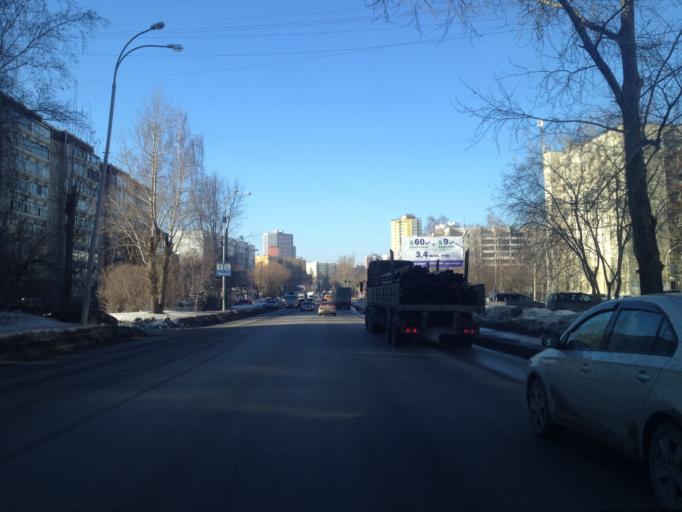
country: RU
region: Sverdlovsk
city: Yekaterinburg
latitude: 56.9011
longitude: 60.6264
